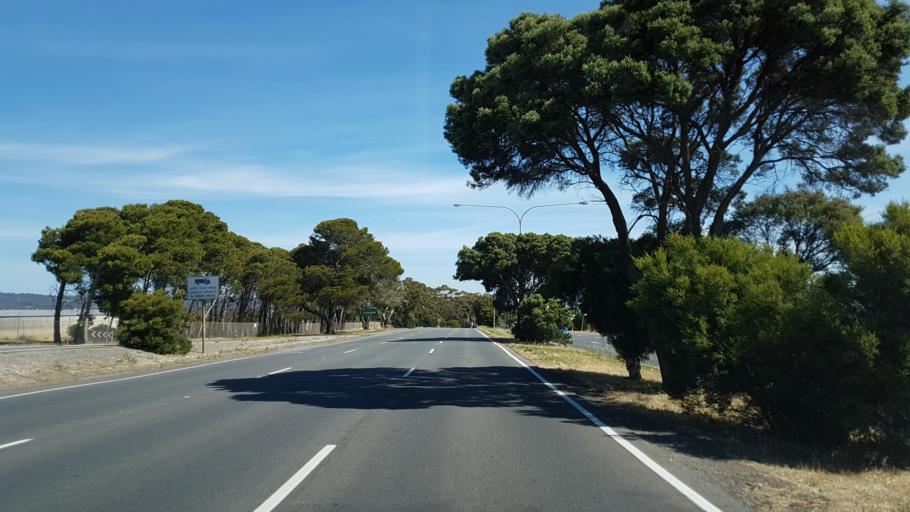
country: AU
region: South Australia
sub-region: Onkaparinga
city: Bedford Park
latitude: -35.0570
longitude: 138.5599
